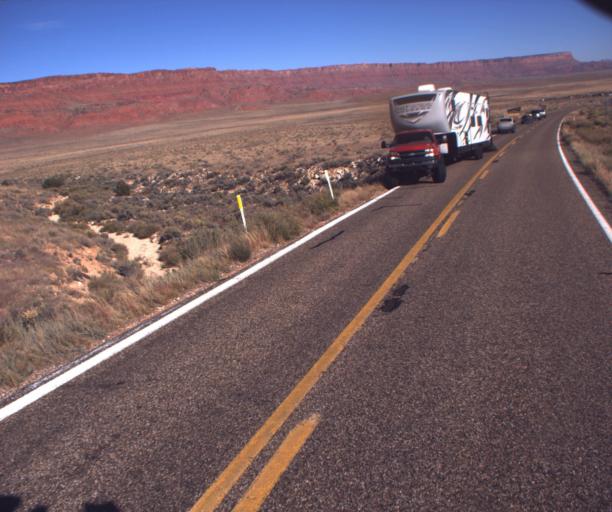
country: US
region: Arizona
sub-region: Coconino County
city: Fredonia
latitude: 36.7336
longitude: -112.0582
